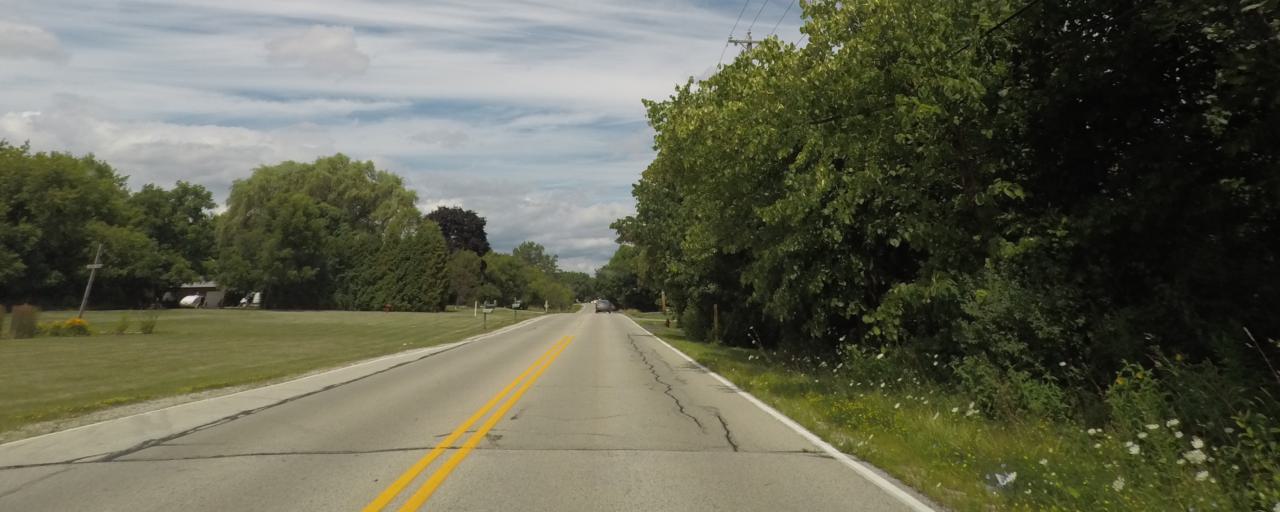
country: US
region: Wisconsin
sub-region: Milwaukee County
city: Hales Corners
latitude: 42.9670
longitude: -88.0691
